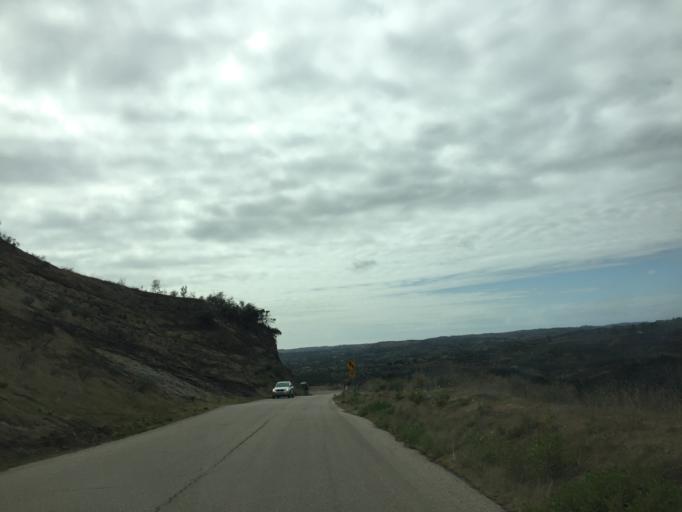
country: US
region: California
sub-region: Santa Barbara County
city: Goleta
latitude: 34.4727
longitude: -119.8011
